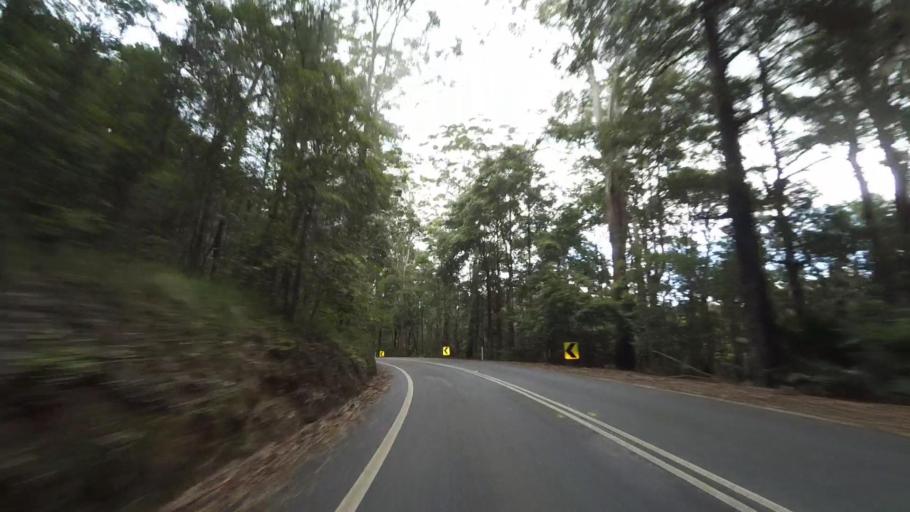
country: AU
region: New South Wales
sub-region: Wollongong
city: Helensburgh
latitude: -34.1634
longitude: 151.0153
